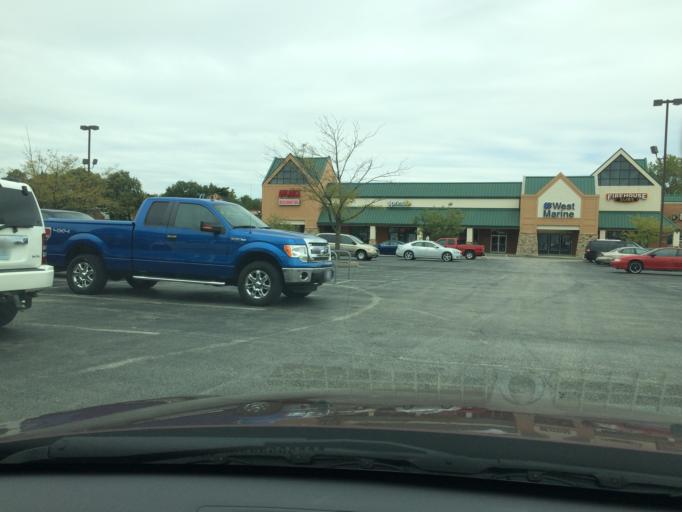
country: US
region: Missouri
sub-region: Saint Charles County
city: Saint Charles
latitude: 38.7713
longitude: -90.4967
